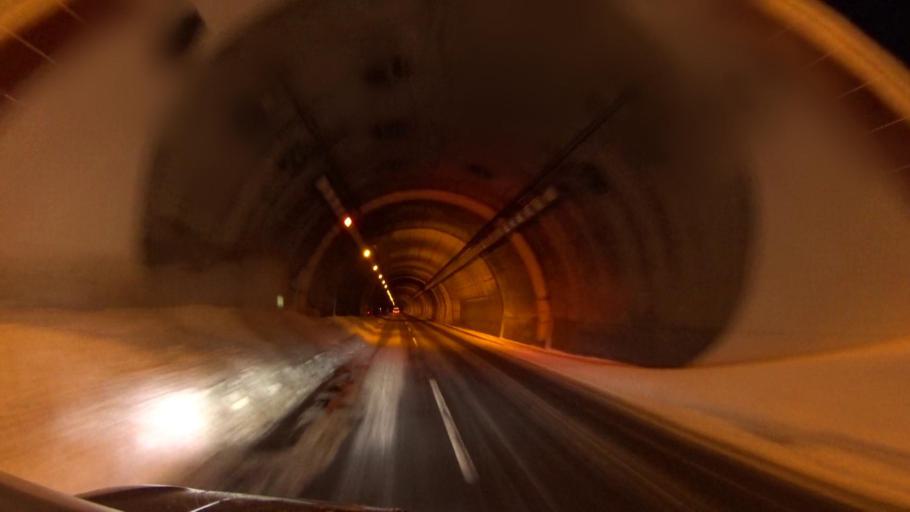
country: JP
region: Hokkaido
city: Otaru
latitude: 43.1763
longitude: 141.0265
